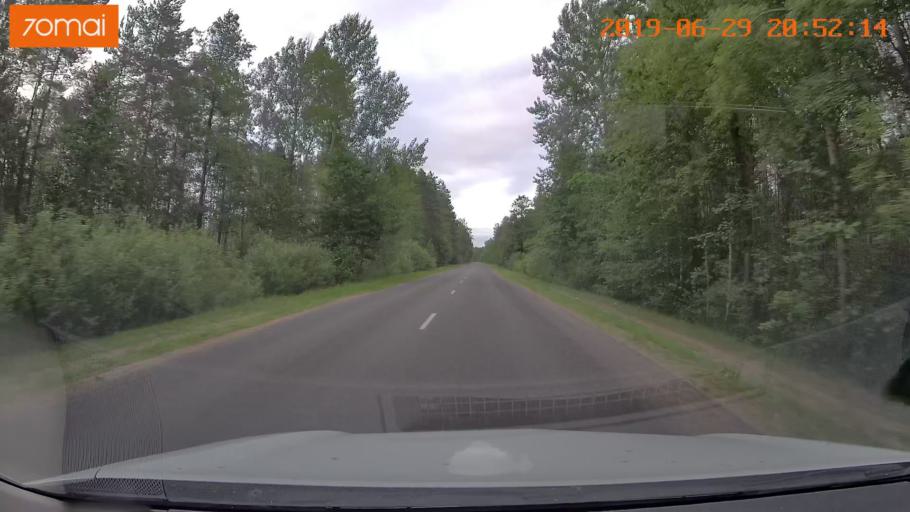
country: BY
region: Brest
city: Hantsavichy
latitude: 52.6973
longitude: 26.3603
